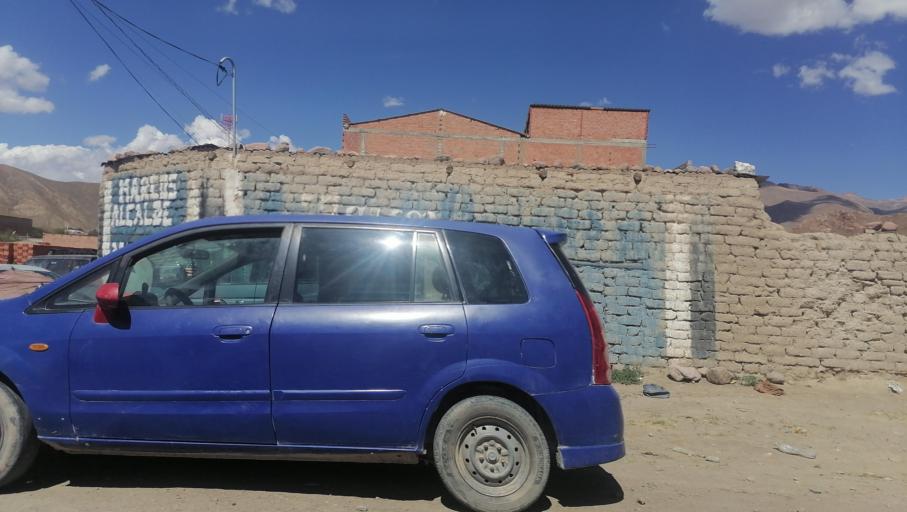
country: BO
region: Oruro
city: Challapata
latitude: -18.9069
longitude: -66.7772
